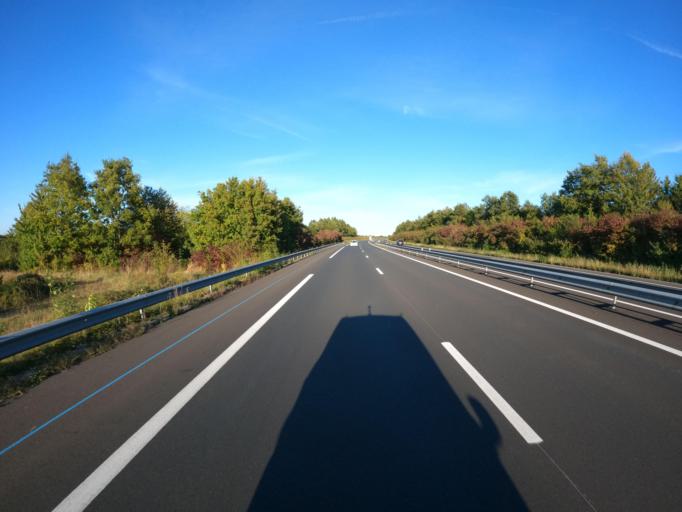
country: FR
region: Pays de la Loire
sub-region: Departement de la Vendee
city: Beaurepaire
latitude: 46.8938
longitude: -1.0901
